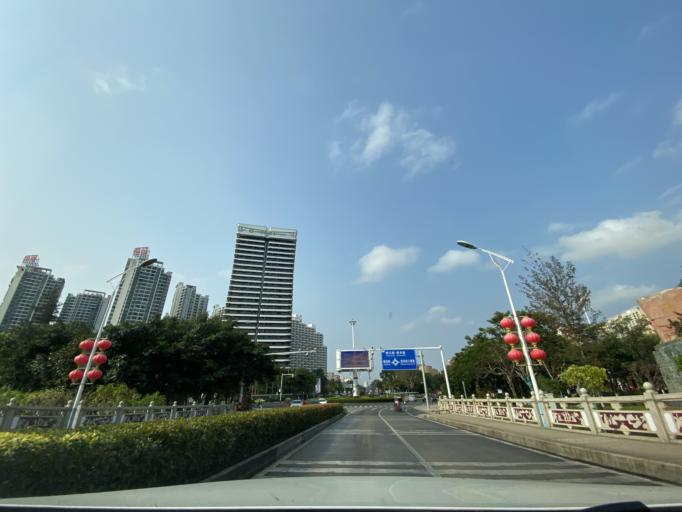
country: CN
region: Hainan
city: Yelin
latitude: 18.5157
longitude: 110.0296
